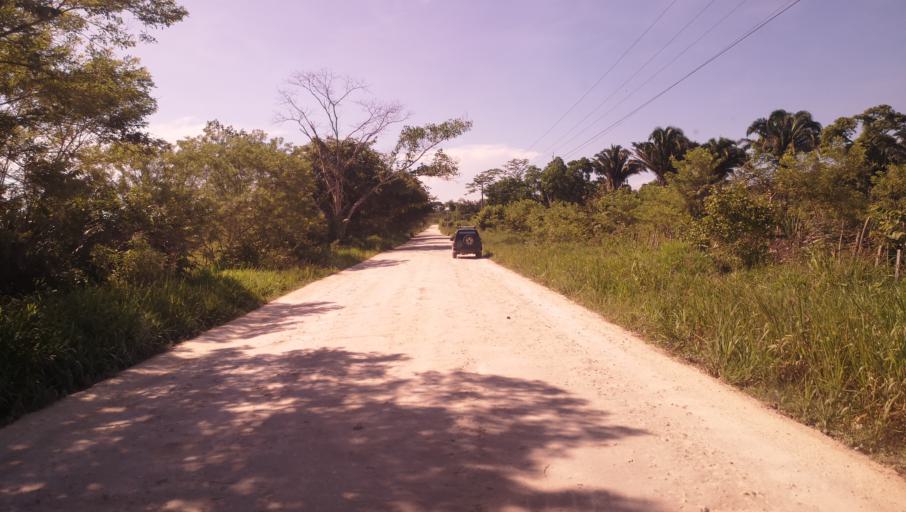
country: GT
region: Peten
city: Dolores
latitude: 16.7186
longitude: -89.3711
